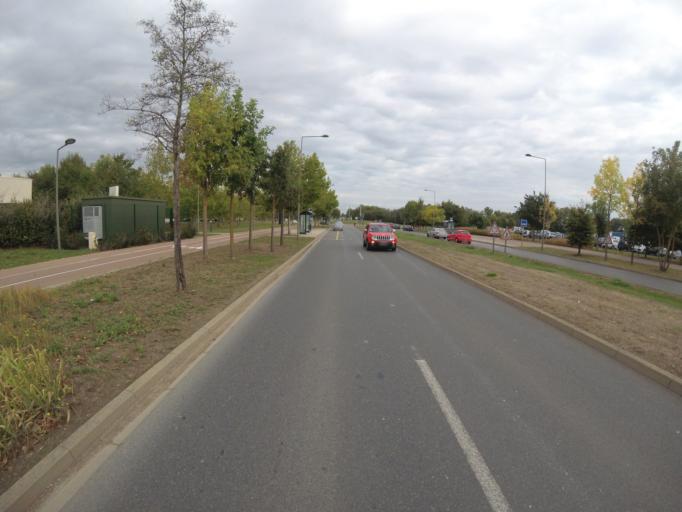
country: FR
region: Ile-de-France
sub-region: Departement de Seine-et-Marne
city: Chanteloup-en-Brie
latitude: 48.8529
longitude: 2.7616
